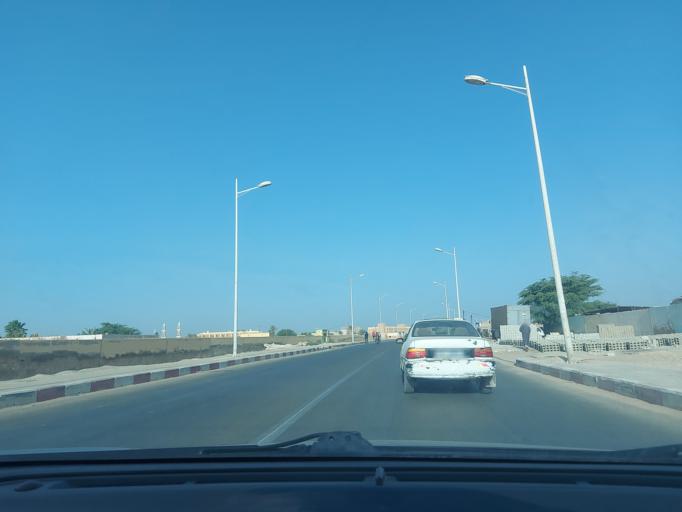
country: MR
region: Nouakchott
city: Nouakchott
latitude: 18.0841
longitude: -15.9955
